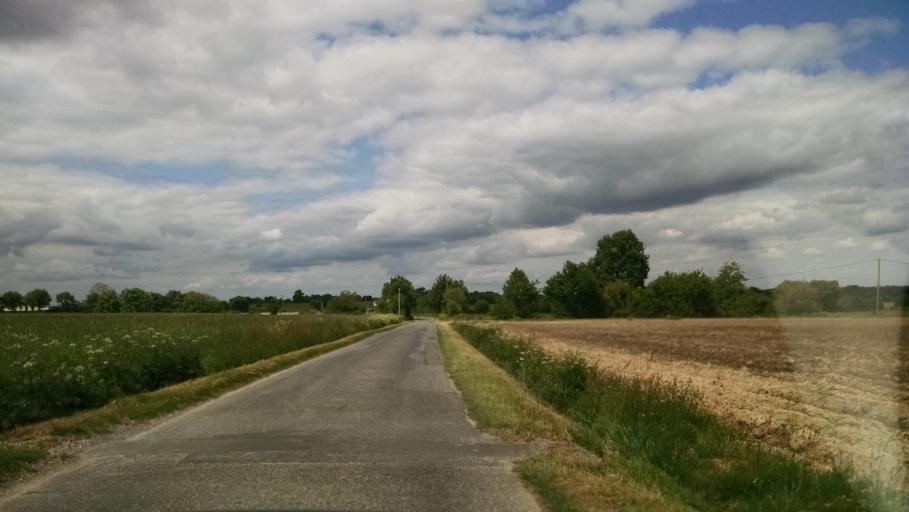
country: FR
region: Pays de la Loire
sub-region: Departement de la Vendee
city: Saint-Hilaire-de-Loulay
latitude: 47.0066
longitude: -1.3728
